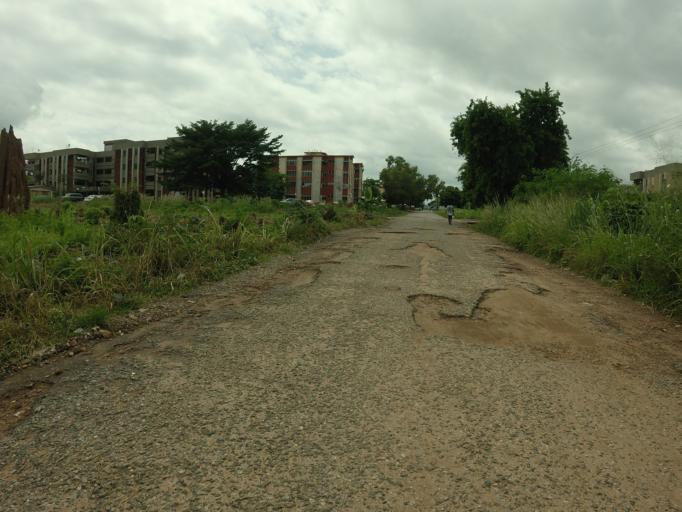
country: GH
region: Volta
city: Ho
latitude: 6.5898
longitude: 0.4606
